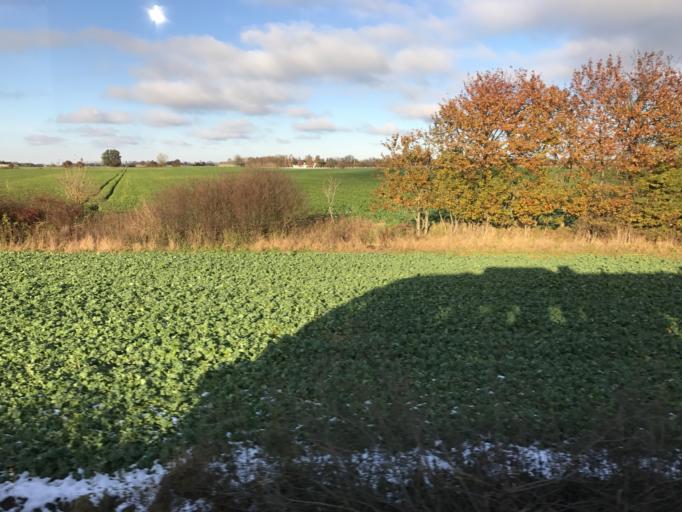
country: DK
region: Zealand
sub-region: Stevns Kommune
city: Harlev
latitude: 55.3558
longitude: 12.2400
